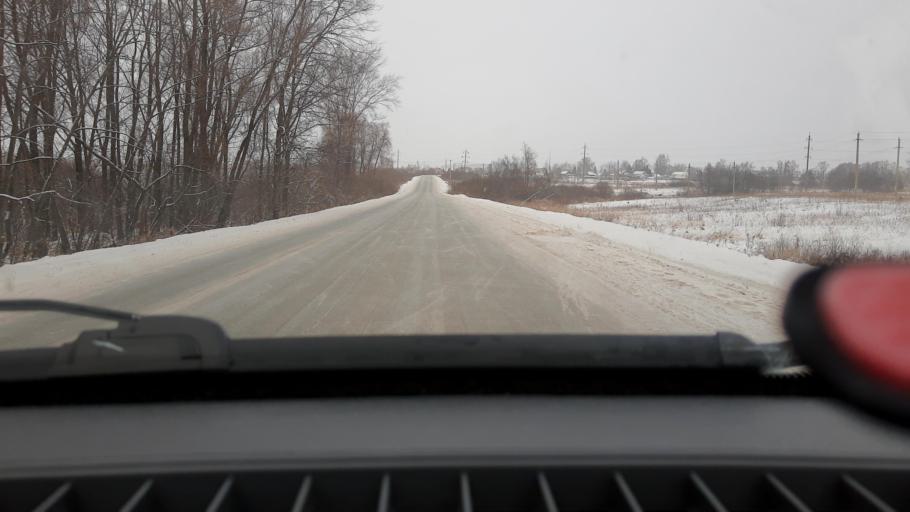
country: RU
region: Bashkortostan
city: Iglino
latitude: 54.7293
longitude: 56.4025
